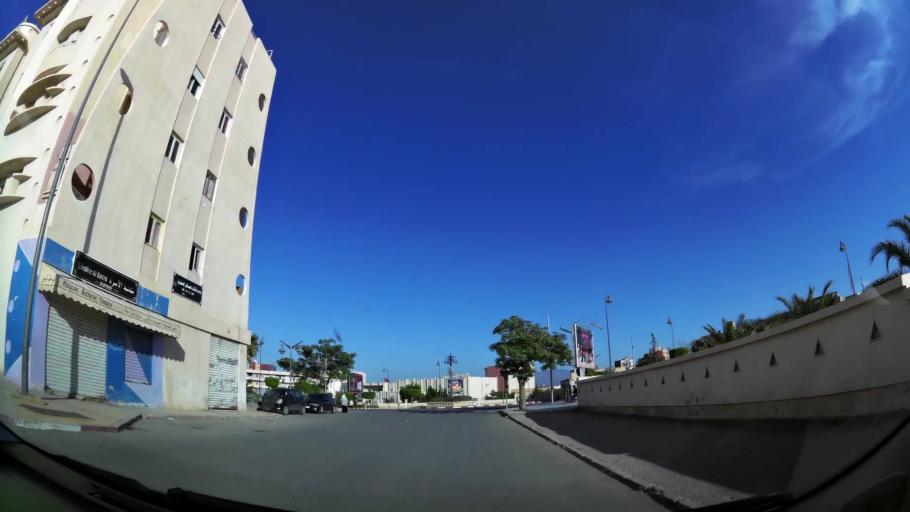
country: MA
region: Oriental
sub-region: Oujda-Angad
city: Oujda
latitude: 34.6917
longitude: -1.9118
